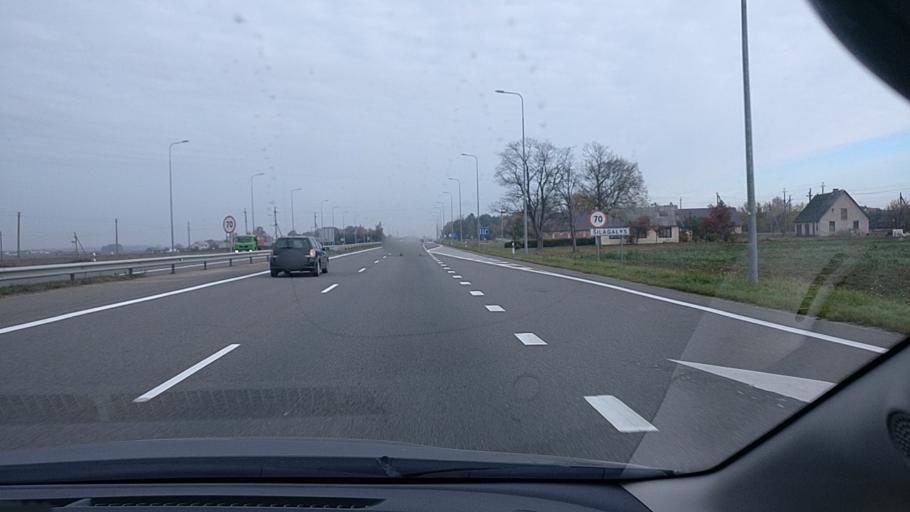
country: LT
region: Panevezys
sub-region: Panevezys City
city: Panevezys
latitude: 55.6695
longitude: 24.3653
